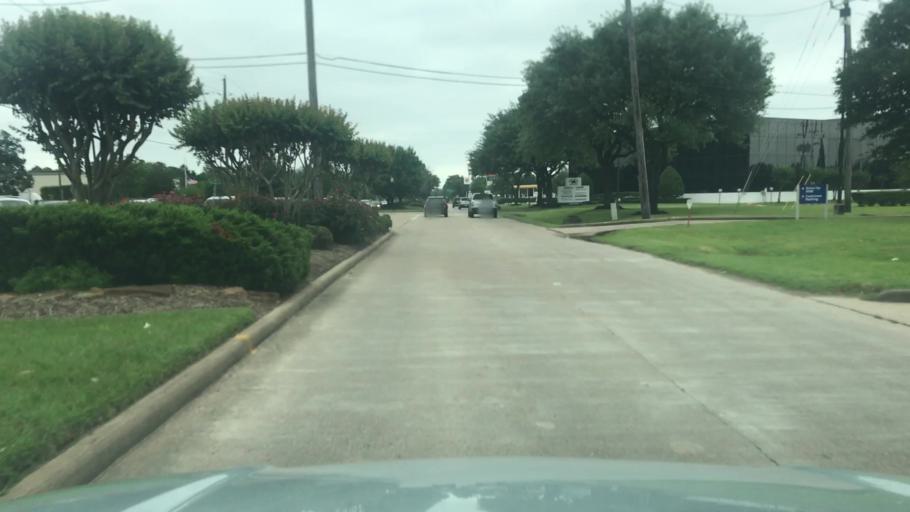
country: US
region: Texas
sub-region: Harris County
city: Katy
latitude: 29.7728
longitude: -95.8183
